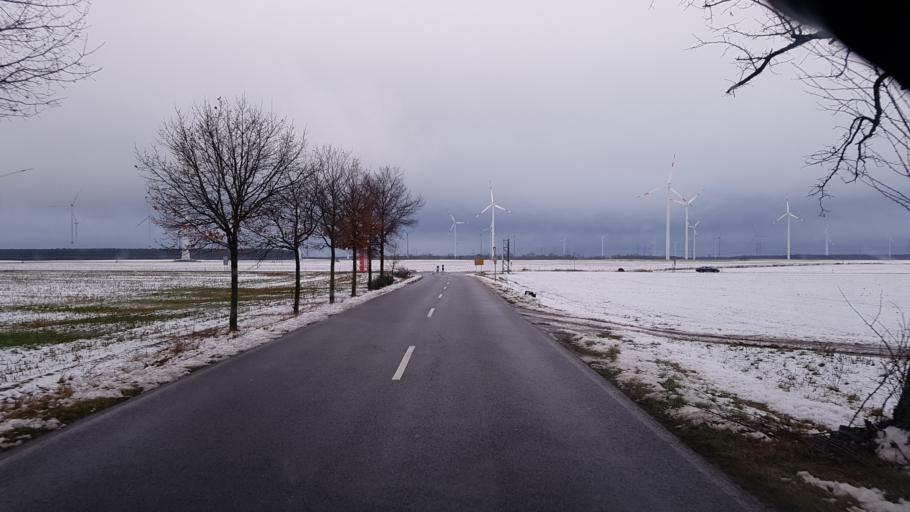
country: DE
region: Brandenburg
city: Luckau
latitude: 51.8849
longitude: 13.7850
